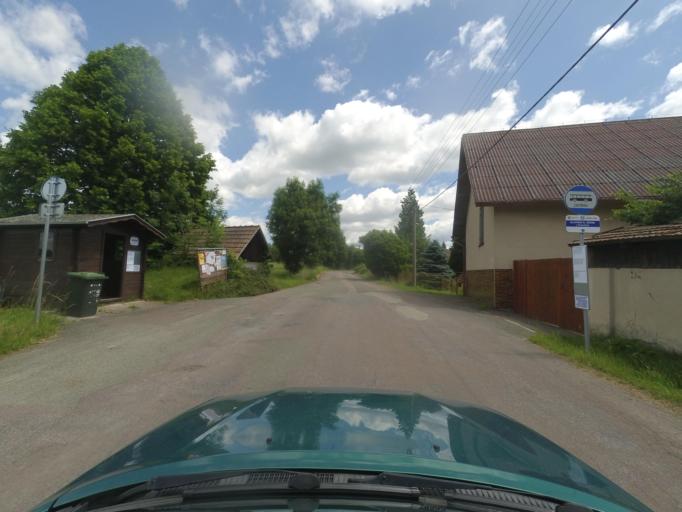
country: CZ
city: Rokytnice v Orlickych Horach
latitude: 50.1320
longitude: 16.4057
